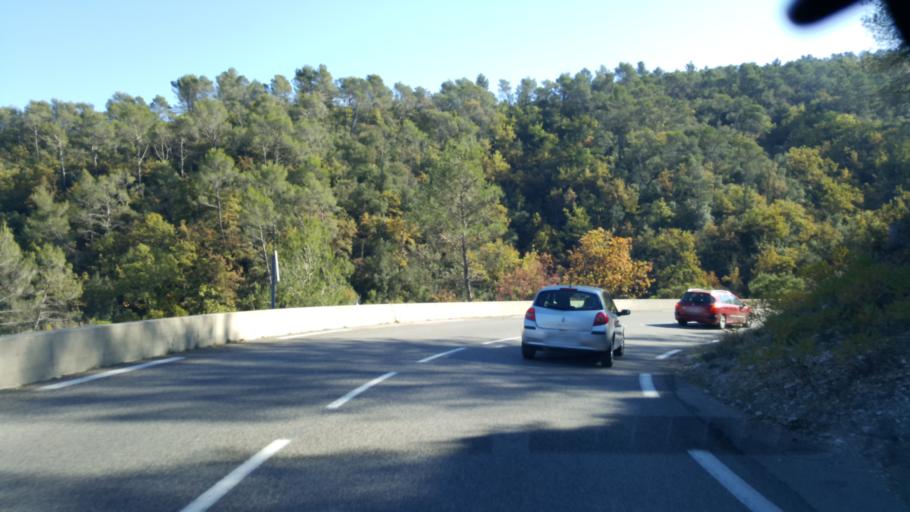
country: FR
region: Provence-Alpes-Cote d'Azur
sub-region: Departement du Var
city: Saint-Zacharie
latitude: 43.3853
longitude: 5.7442
